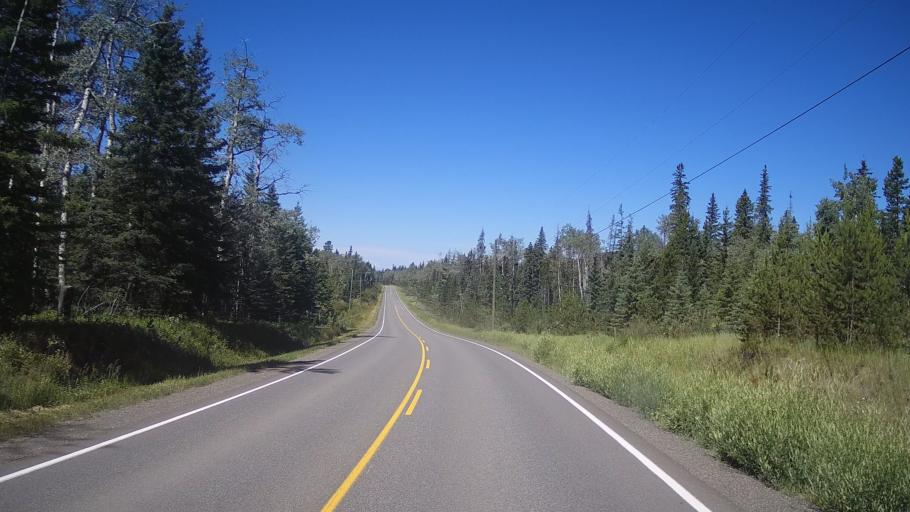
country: CA
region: British Columbia
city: Cache Creek
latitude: 51.5474
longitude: -121.0797
